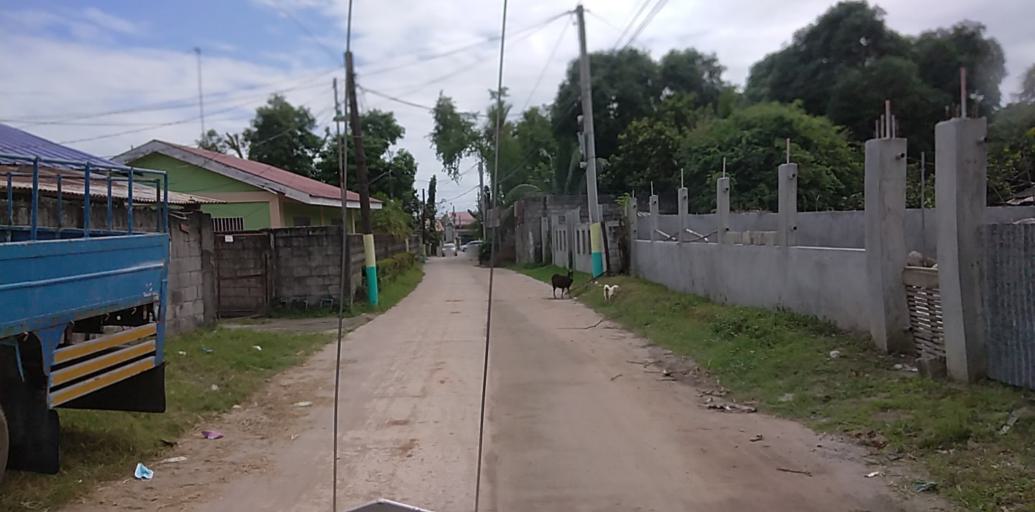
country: PH
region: Central Luzon
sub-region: Province of Pampanga
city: Porac
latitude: 15.0634
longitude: 120.5408
